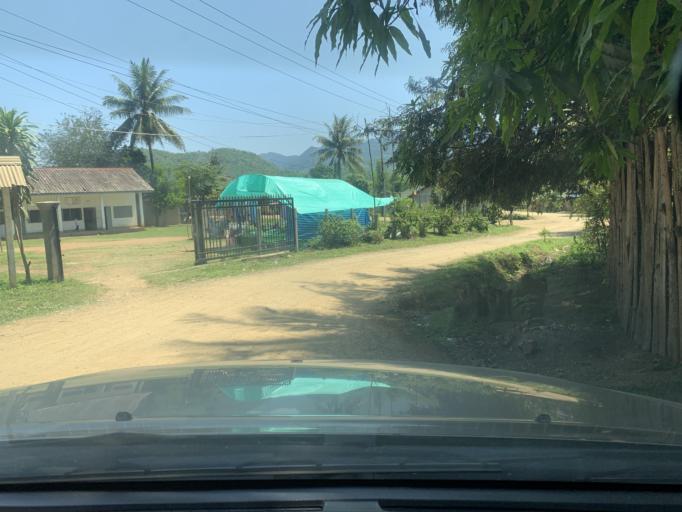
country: LA
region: Louangphabang
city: Louangphabang
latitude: 19.9058
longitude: 102.2286
